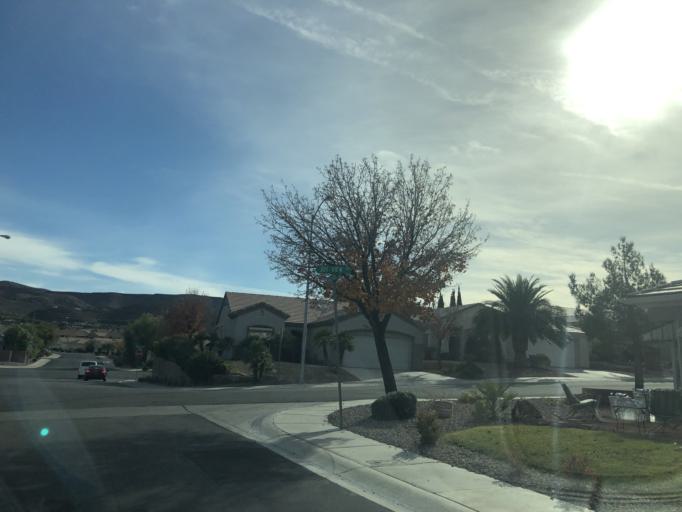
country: US
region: Nevada
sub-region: Clark County
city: Whitney
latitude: 36.0062
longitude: -115.0719
